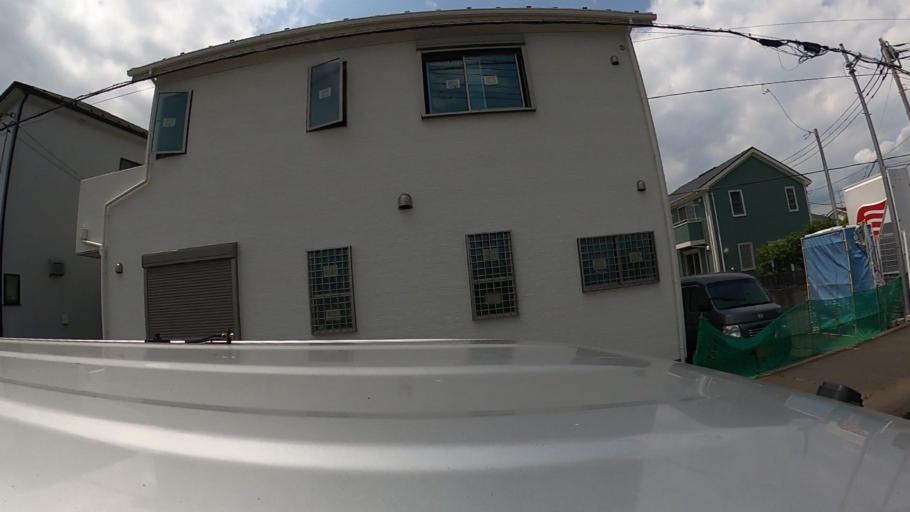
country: JP
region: Kanagawa
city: Chigasaki
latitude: 35.3776
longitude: 139.3972
